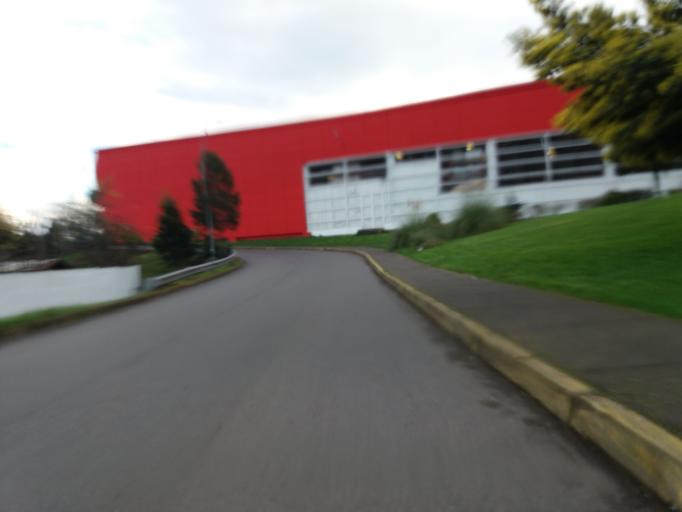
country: CL
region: Araucania
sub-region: Provincia de Cautin
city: Temuco
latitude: -38.7466
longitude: -72.6057
